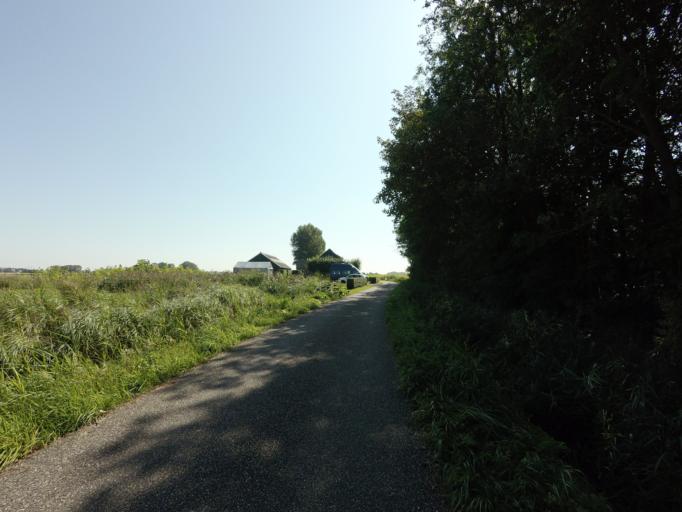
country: NL
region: Friesland
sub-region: Gemeente Dongeradeel
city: Holwerd
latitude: 53.3666
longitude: 5.9261
